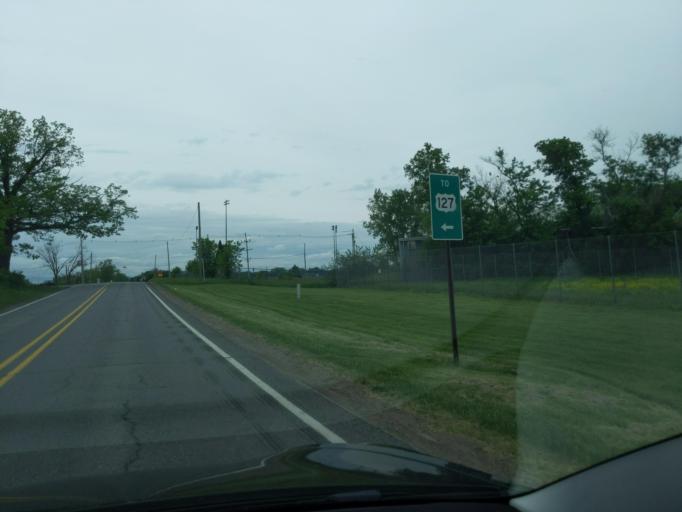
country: US
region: Michigan
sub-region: Ingham County
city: Mason
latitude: 42.5664
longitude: -84.4340
